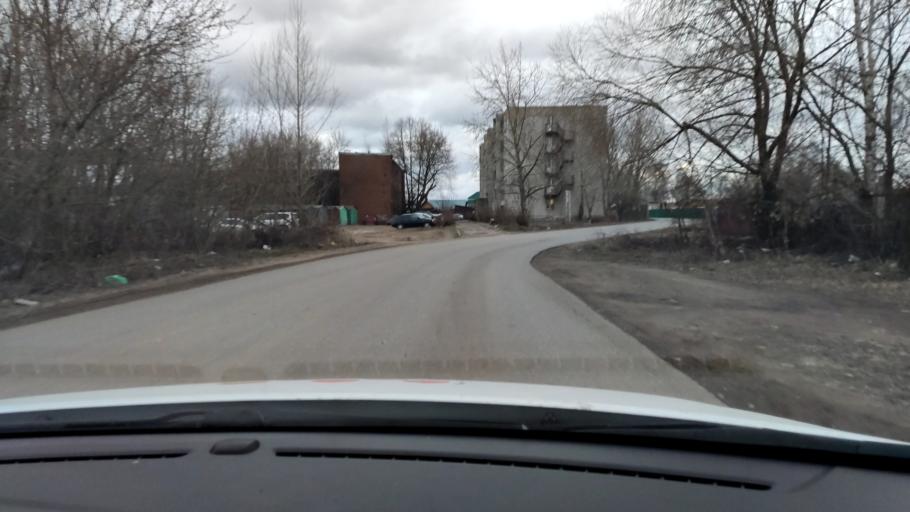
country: RU
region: Tatarstan
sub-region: Gorod Kazan'
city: Kazan
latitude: 55.7202
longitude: 49.0928
